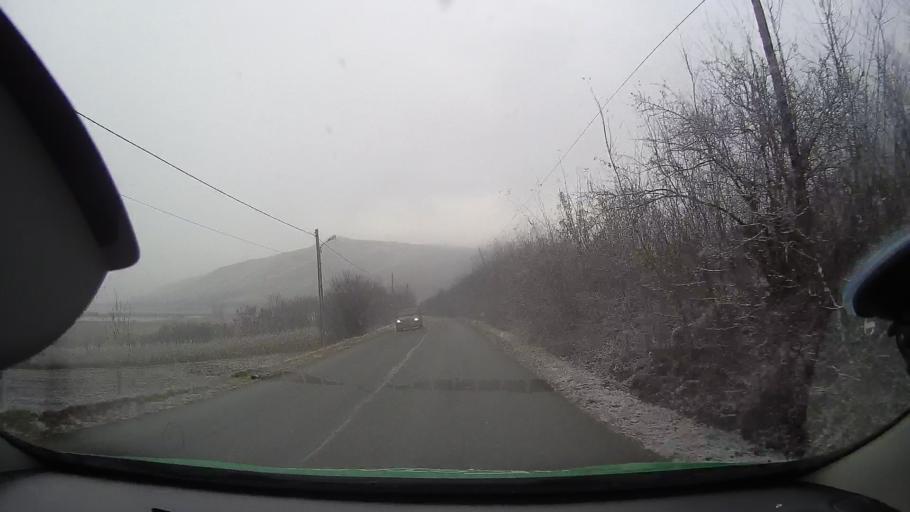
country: RO
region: Alba
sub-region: Comuna Noslac
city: Noslac
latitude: 46.3625
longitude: 23.9317
